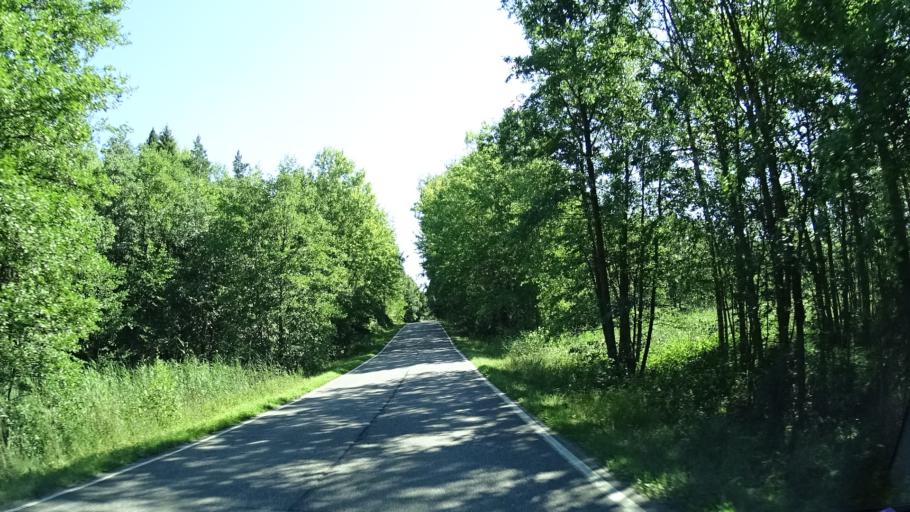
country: FI
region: Varsinais-Suomi
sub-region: Turku
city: Merimasku
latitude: 60.4973
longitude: 21.7798
